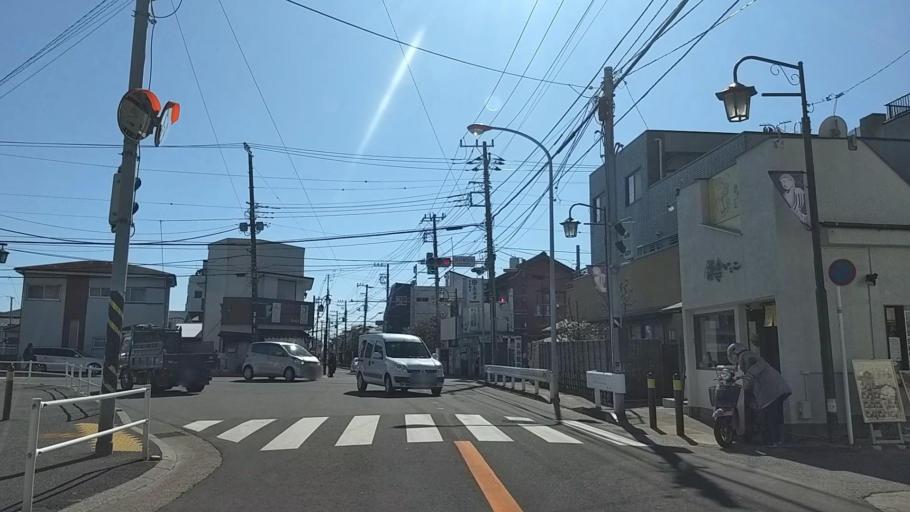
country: JP
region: Kanagawa
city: Kamakura
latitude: 35.3131
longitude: 139.5352
